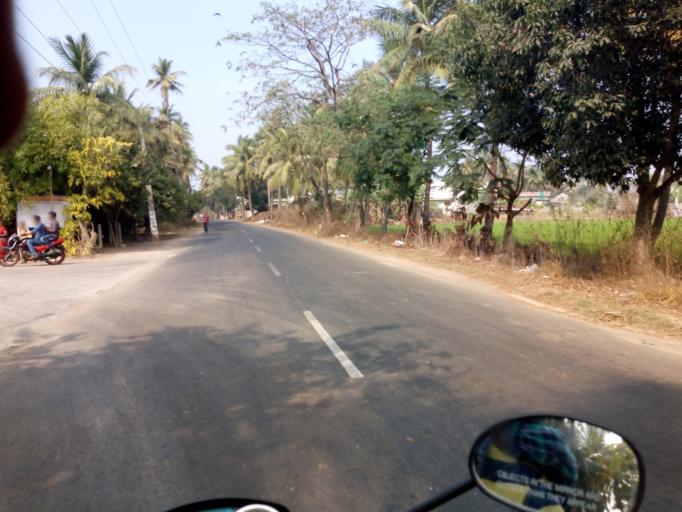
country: IN
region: Andhra Pradesh
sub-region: West Godavari
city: Palakollu
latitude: 16.5871
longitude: 81.6439
